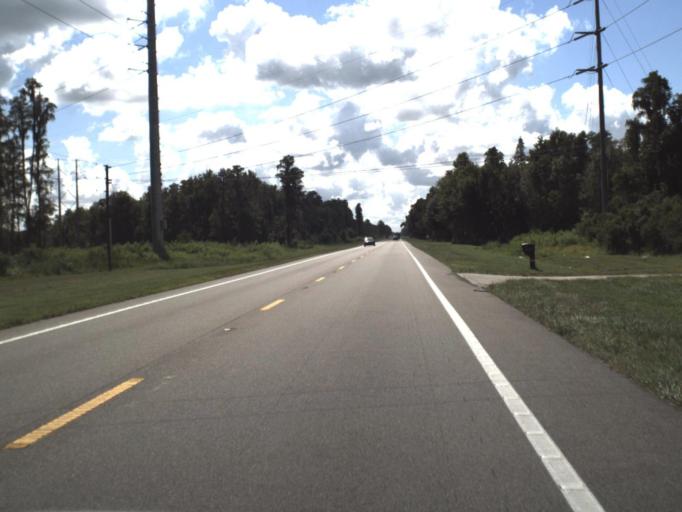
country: US
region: Florida
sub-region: Polk County
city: Kathleen
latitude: 28.2285
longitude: -82.0331
